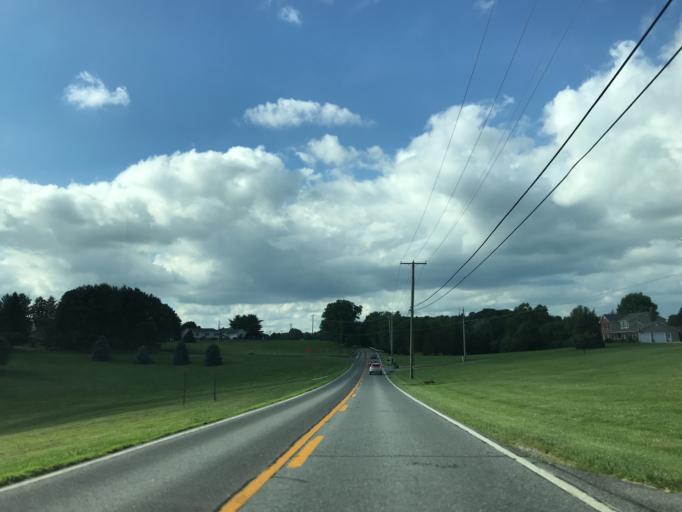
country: US
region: Maryland
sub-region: Carroll County
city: Hampstead
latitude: 39.6261
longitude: -76.7943
